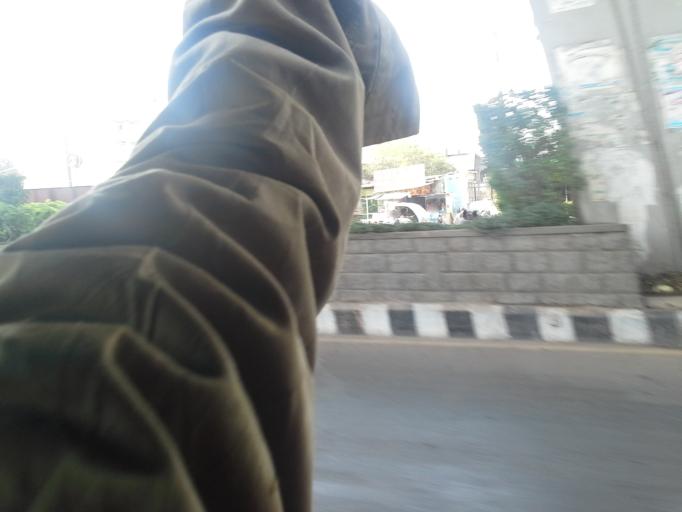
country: IN
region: Telangana
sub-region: Hyderabad
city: Hyderabad
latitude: 17.3461
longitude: 78.4159
